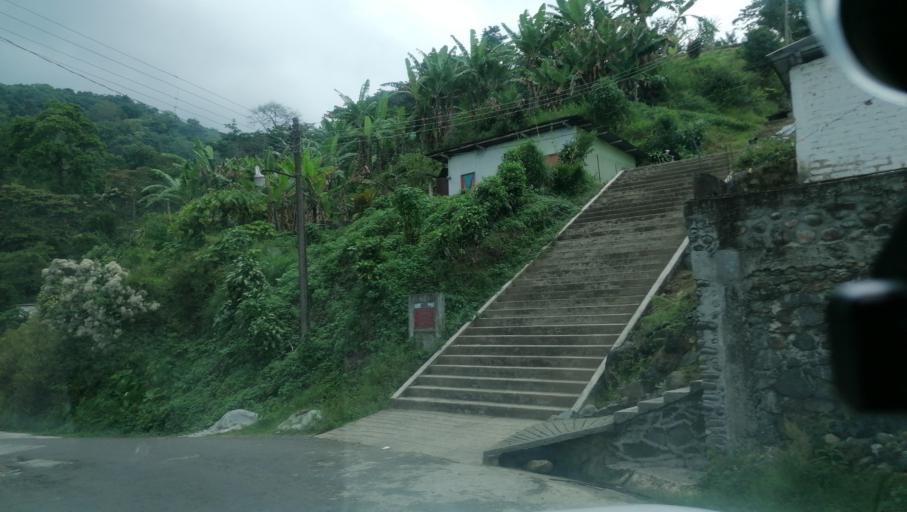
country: MX
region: Chiapas
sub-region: Cacahoatan
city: Benito Juarez
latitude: 15.0757
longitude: -92.1721
